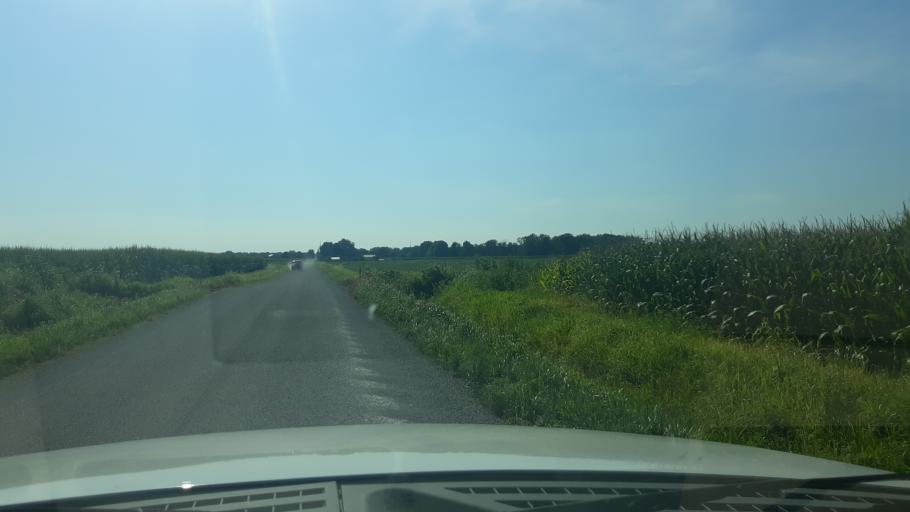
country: US
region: Illinois
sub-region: Saline County
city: Eldorado
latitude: 37.8631
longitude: -88.4957
